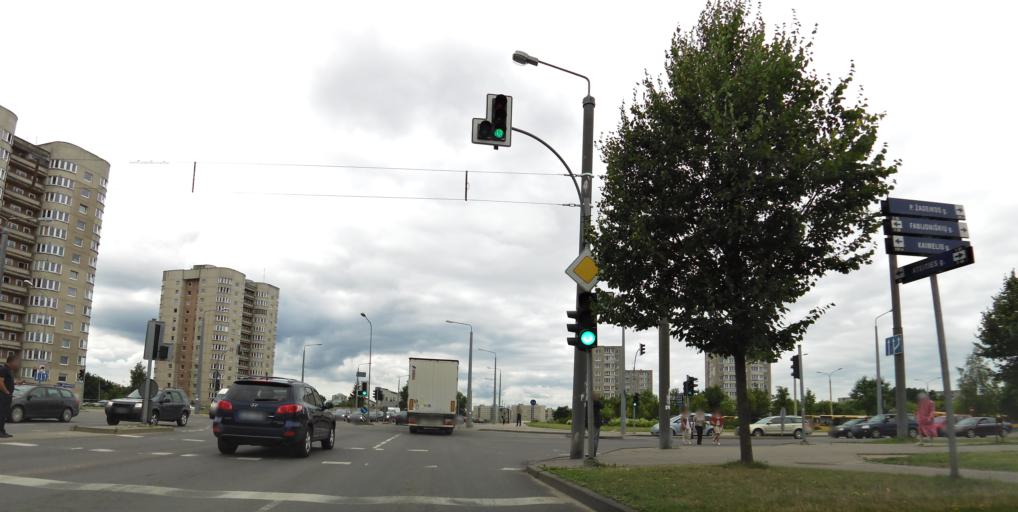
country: LT
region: Vilnius County
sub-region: Vilnius
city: Fabijoniskes
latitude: 54.7305
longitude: 25.2459
